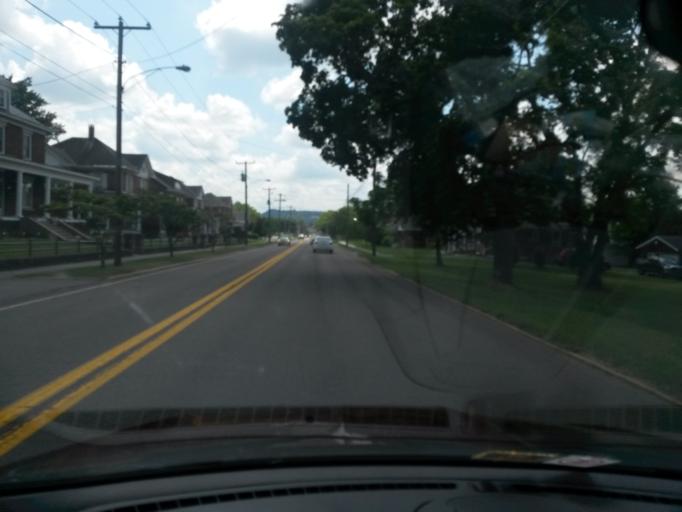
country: US
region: West Virginia
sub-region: Mercer County
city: Princeton
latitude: 37.3680
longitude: -81.1062
